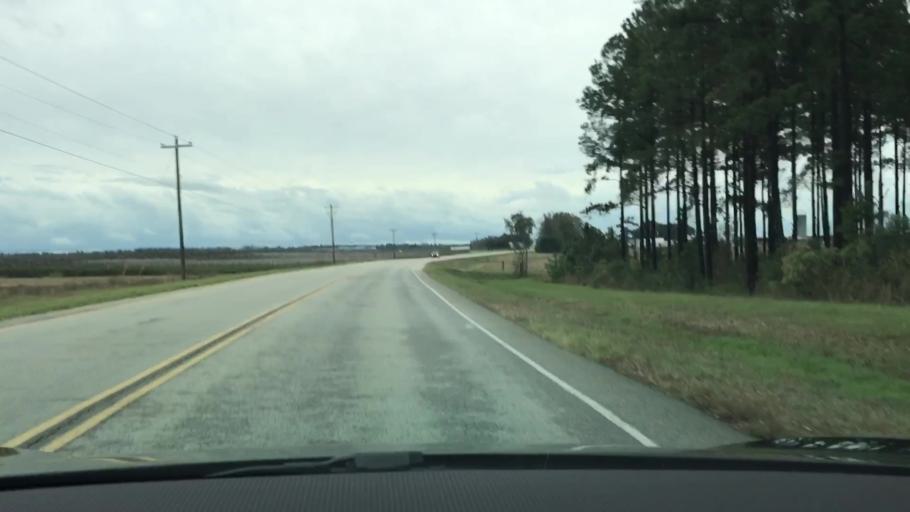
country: US
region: Georgia
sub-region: Jefferson County
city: Wrens
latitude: 33.1127
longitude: -82.4305
